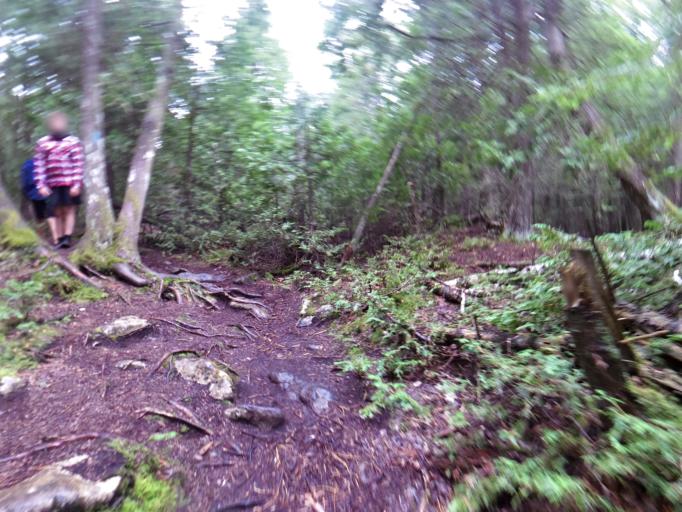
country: CA
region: Ontario
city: Tobermory
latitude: 45.2620
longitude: -81.6449
